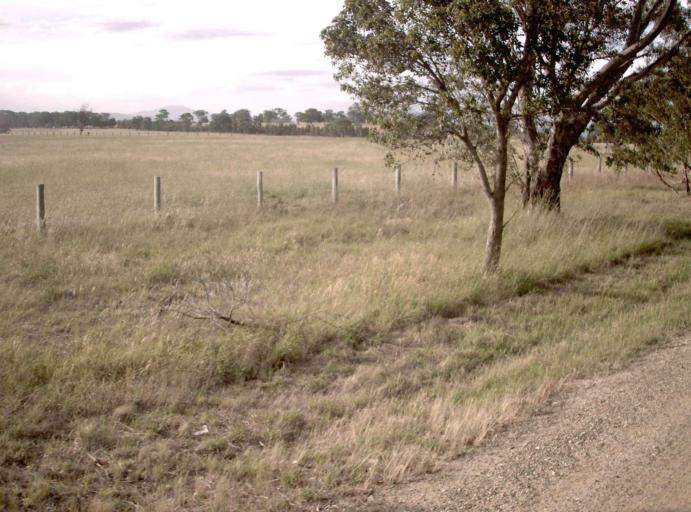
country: AU
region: Victoria
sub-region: Wellington
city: Sale
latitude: -37.9331
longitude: 146.9913
